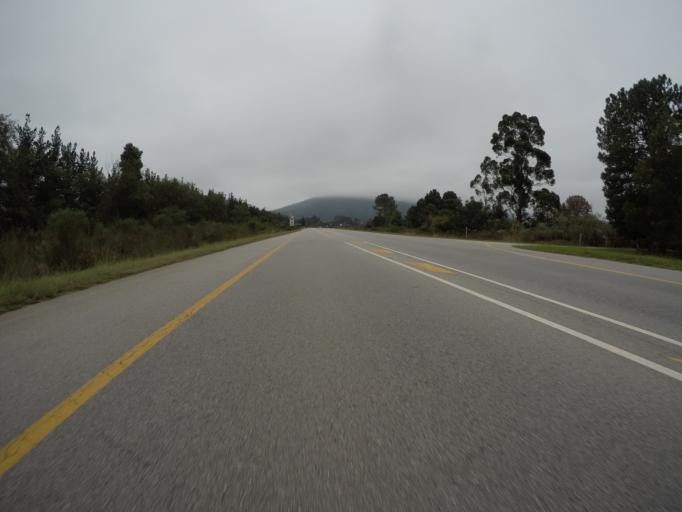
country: ZA
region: Western Cape
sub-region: Eden District Municipality
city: Plettenberg Bay
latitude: -33.9398
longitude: 23.4892
